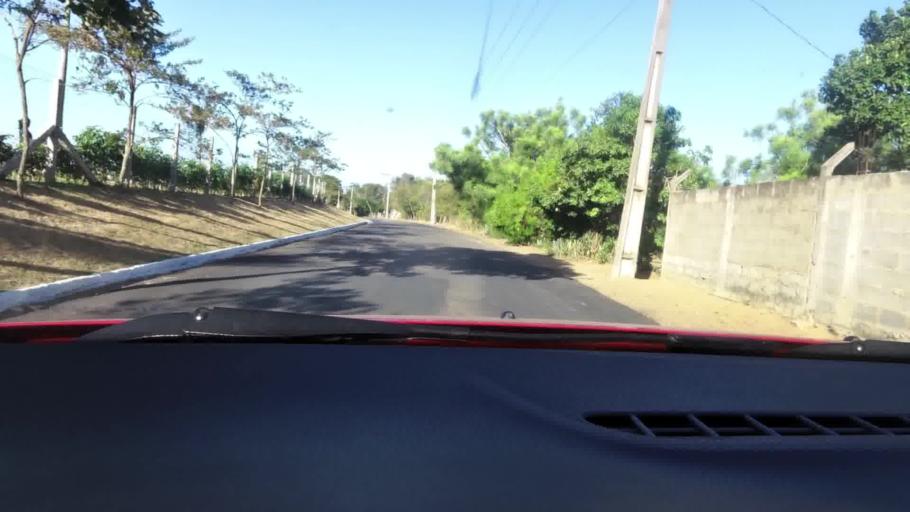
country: BR
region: Espirito Santo
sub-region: Guarapari
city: Guarapari
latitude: -20.5313
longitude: -40.4617
